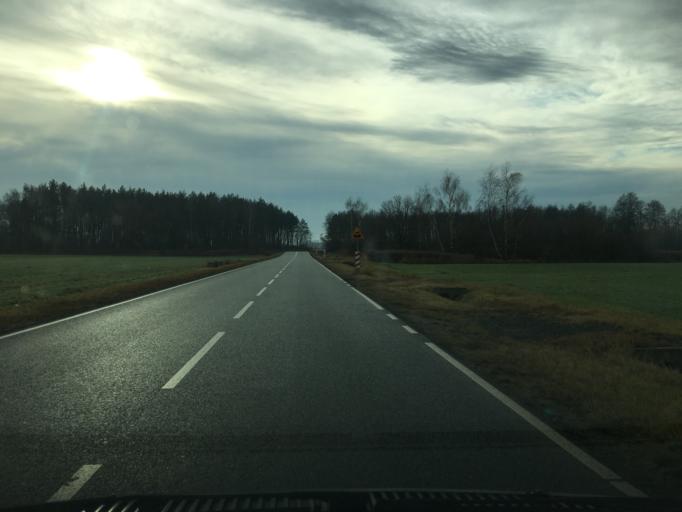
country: PL
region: Lower Silesian Voivodeship
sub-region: Powiat wroclawski
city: Dlugoleka
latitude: 51.1797
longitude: 17.2226
